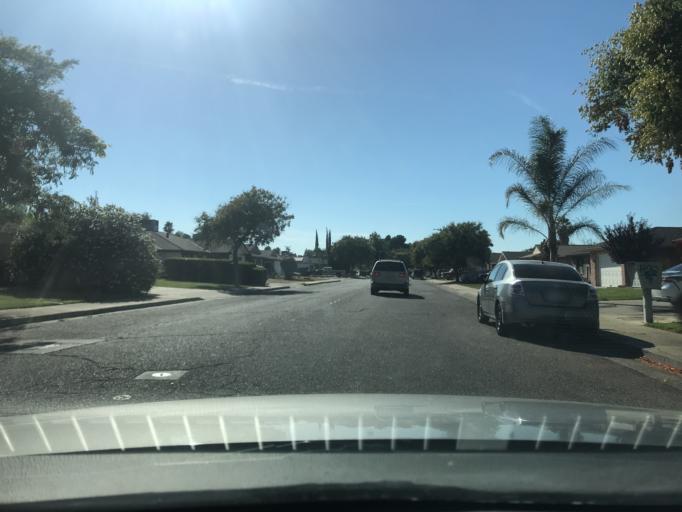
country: US
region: California
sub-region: Merced County
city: Atwater
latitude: 37.3499
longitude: -120.5971
